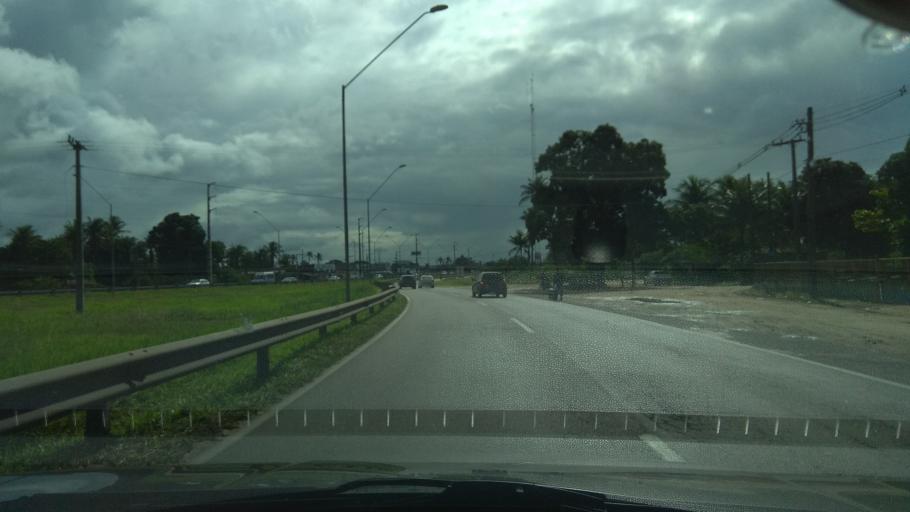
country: BR
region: Bahia
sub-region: Feira De Santana
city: Feira de Santana
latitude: -12.3185
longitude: -38.8738
